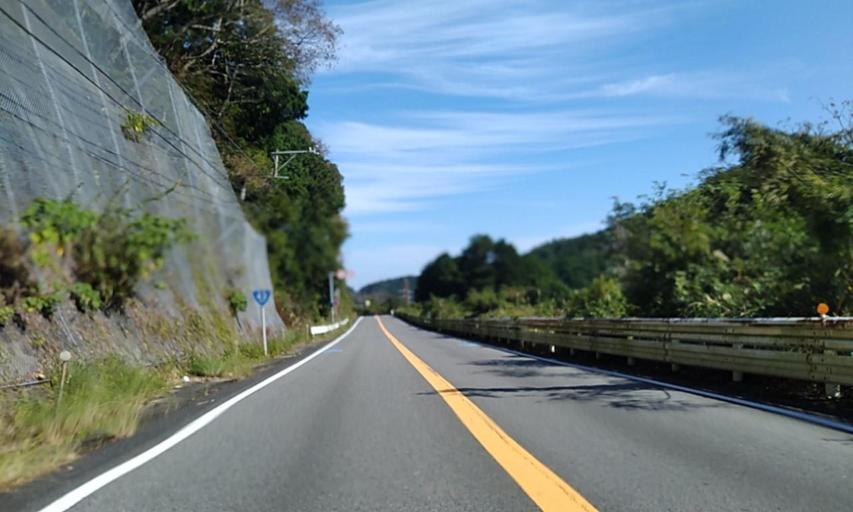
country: JP
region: Mie
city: Owase
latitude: 34.1588
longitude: 136.2692
